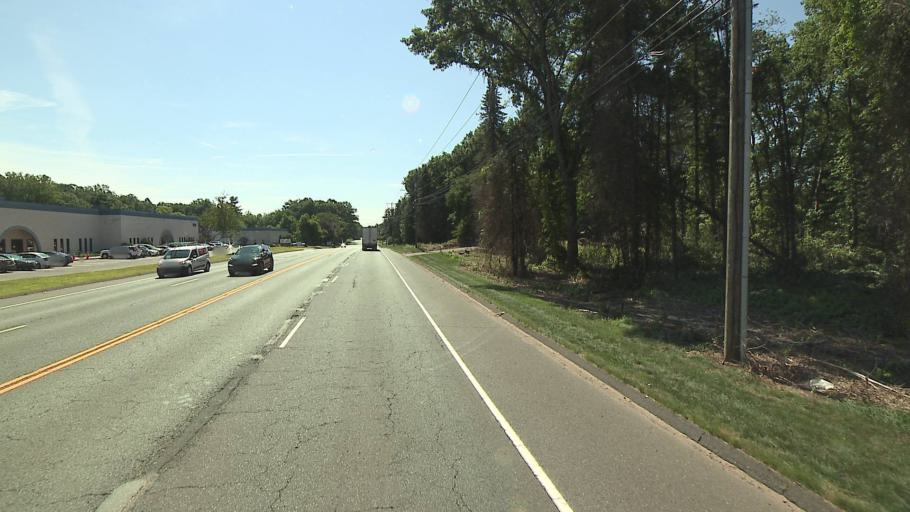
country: US
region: Connecticut
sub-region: Hartford County
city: Blue Hills
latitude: 41.8613
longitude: -72.7130
